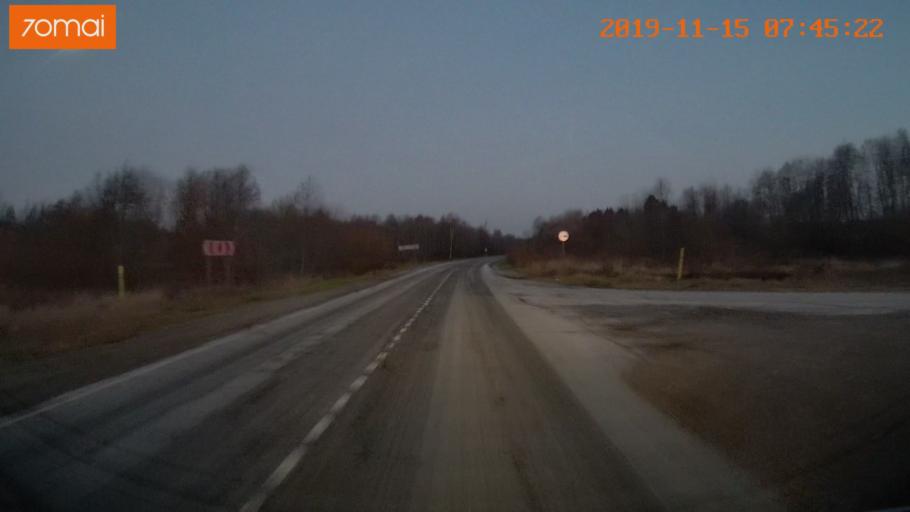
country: RU
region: Vologda
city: Sheksna
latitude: 58.8228
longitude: 38.2987
